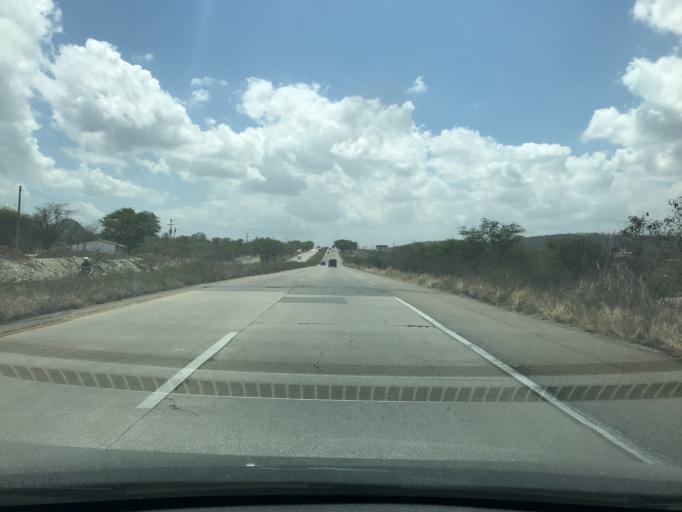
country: BR
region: Pernambuco
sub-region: Bezerros
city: Bezerros
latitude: -8.2979
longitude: -35.8622
